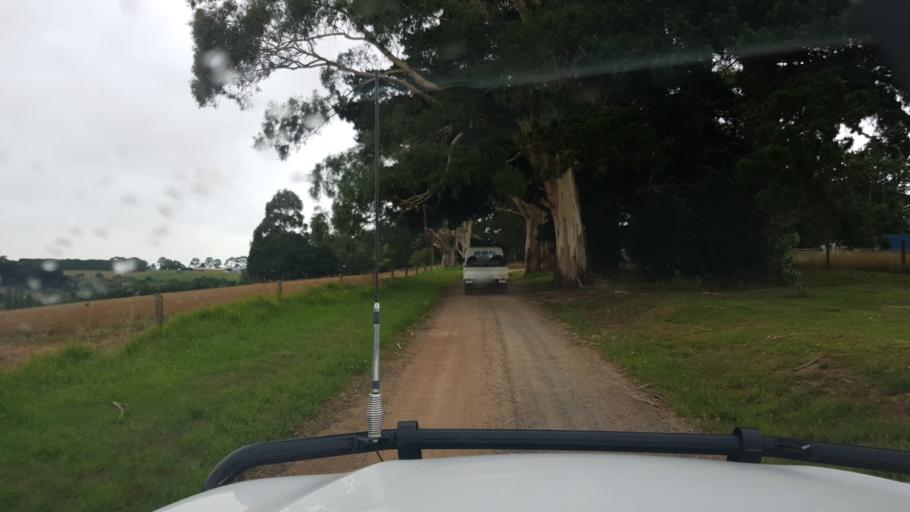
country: AU
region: Victoria
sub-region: Baw Baw
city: Warragul
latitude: -38.2458
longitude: 145.9222
